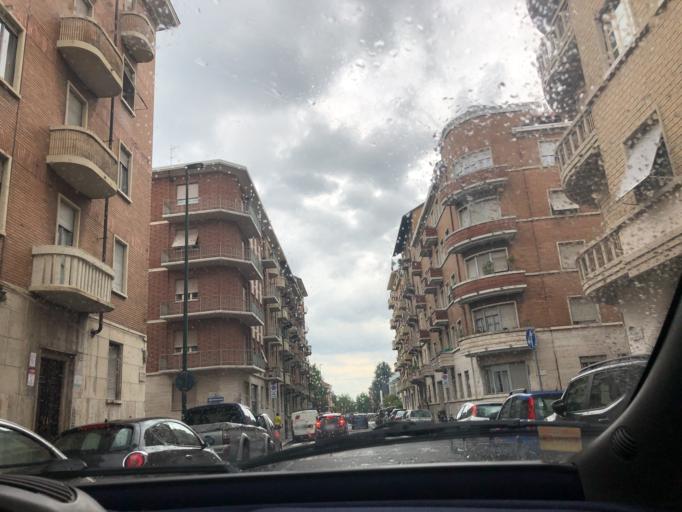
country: IT
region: Piedmont
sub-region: Provincia di Torino
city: Lesna
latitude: 45.0822
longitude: 7.6451
